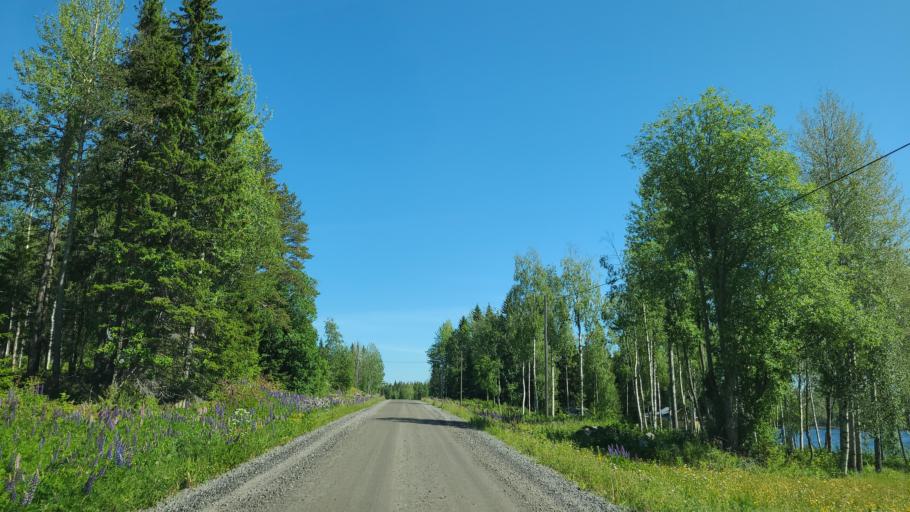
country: SE
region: Vaesterbotten
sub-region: Bjurholms Kommun
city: Bjurholm
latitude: 63.6405
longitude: 19.1395
